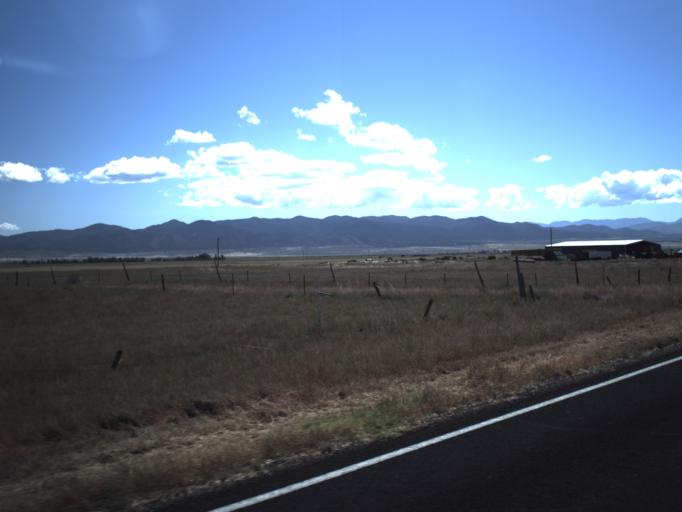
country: US
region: Utah
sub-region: Washington County
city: Enterprise
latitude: 37.6817
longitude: -113.6565
